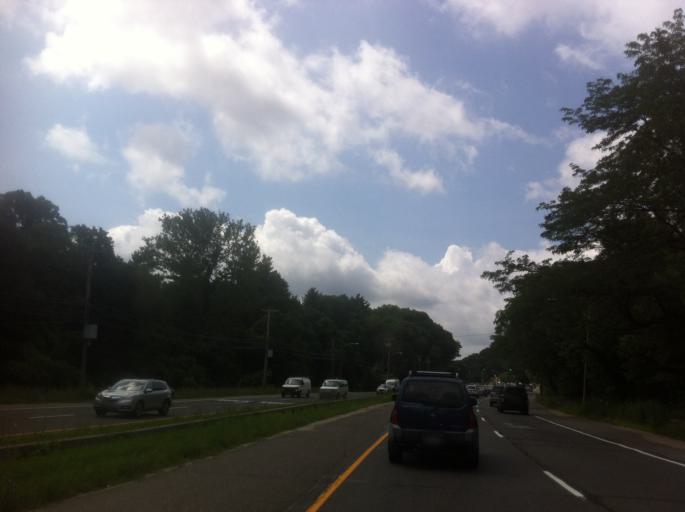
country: US
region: New York
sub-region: Nassau County
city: Glen Head
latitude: 40.8463
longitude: -73.6158
